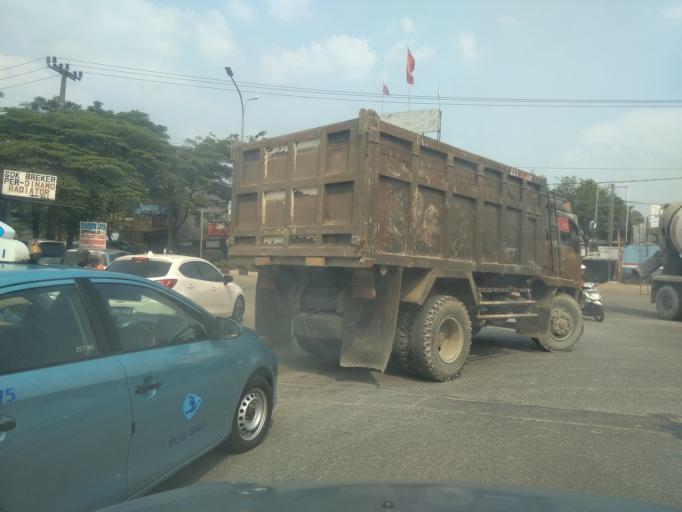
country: ID
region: West Java
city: Serpong
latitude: -6.3117
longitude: 106.6894
